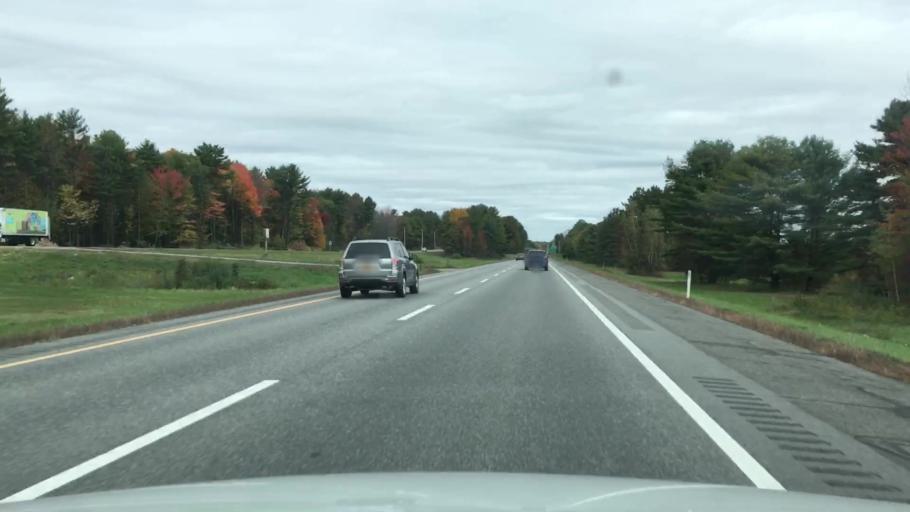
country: US
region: Maine
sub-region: Kennebec County
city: Oakland
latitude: 44.4981
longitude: -69.7041
